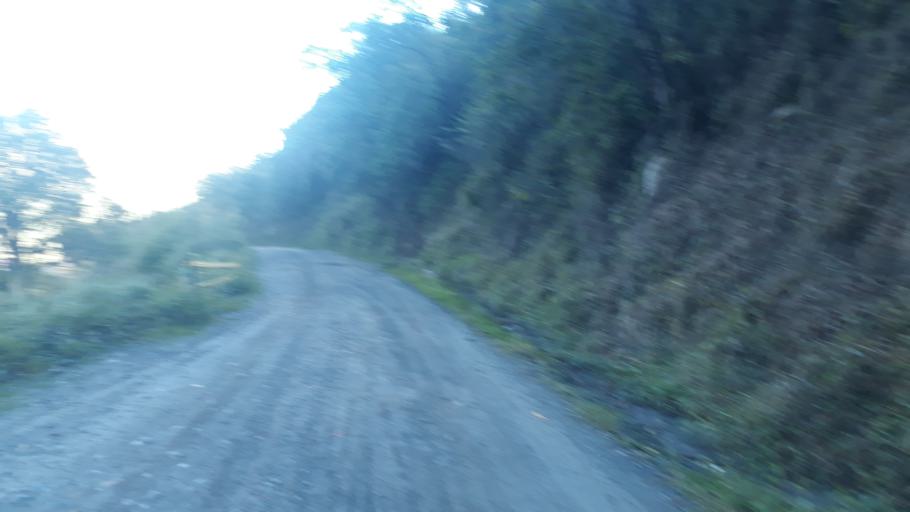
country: CO
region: Boyaca
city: San Mateo
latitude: 6.4009
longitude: -72.5594
